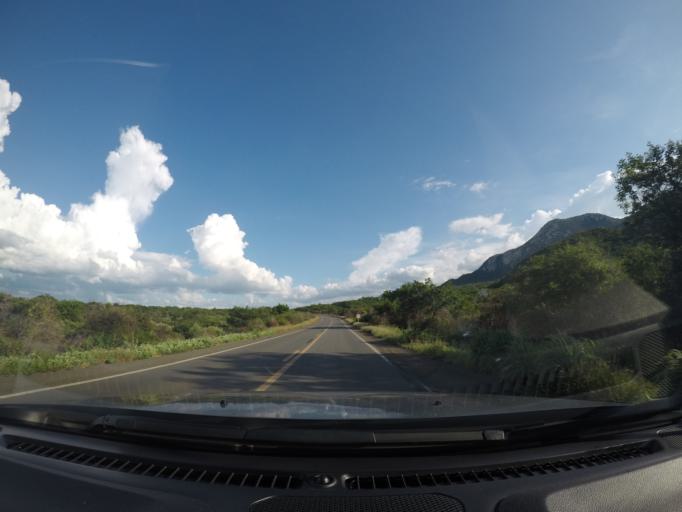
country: BR
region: Bahia
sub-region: Oliveira Dos Brejinhos
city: Oliveira dos Brejinhos
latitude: -12.0650
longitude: -42.9592
